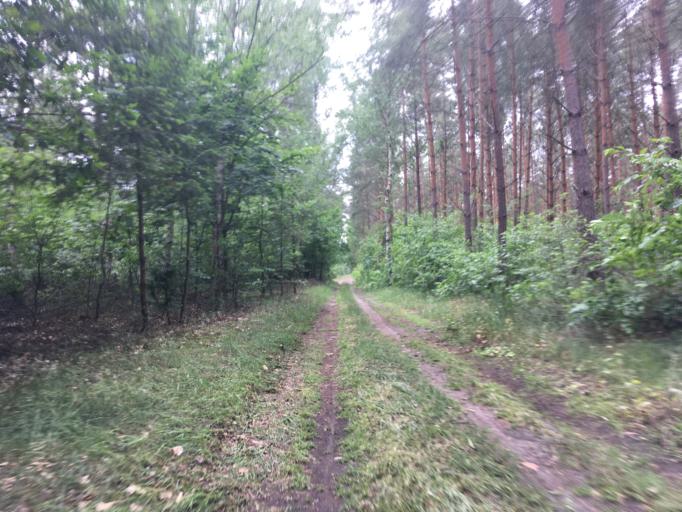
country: DE
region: Berlin
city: Rahnsdorf
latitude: 52.4208
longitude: 13.7021
